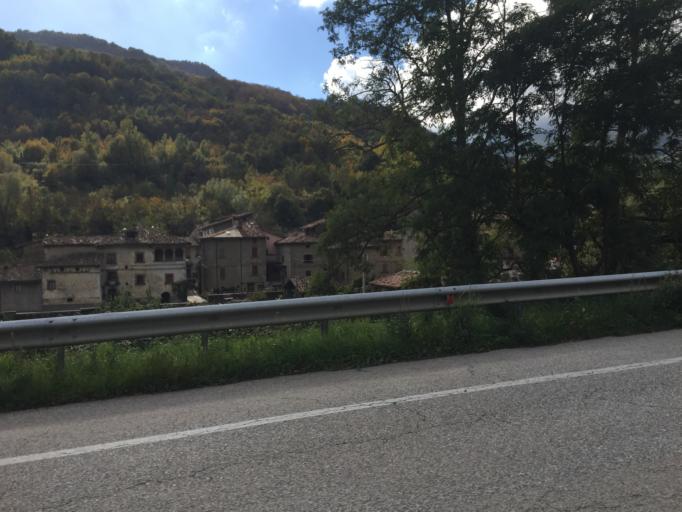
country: IT
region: The Marches
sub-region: Provincia di Ascoli Piceno
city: Arquata del Tronto
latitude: 42.7736
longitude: 13.3148
